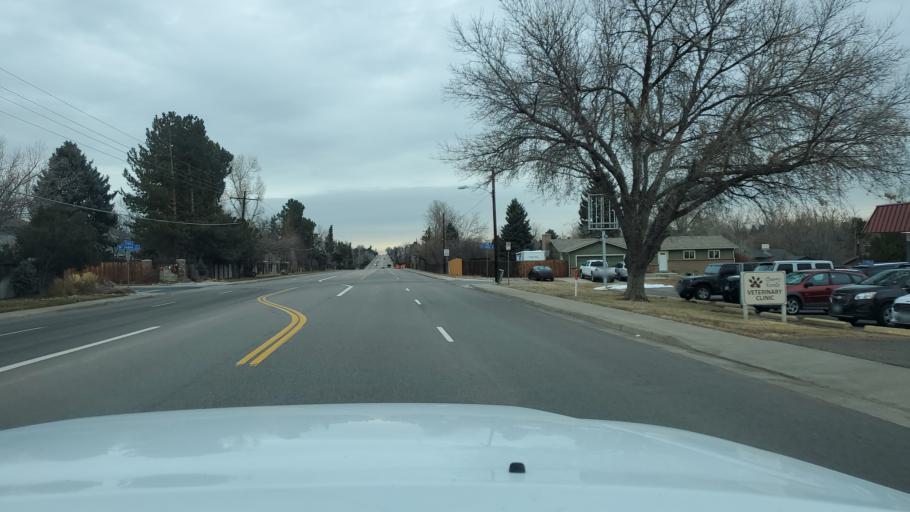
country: US
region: Colorado
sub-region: Arapahoe County
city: Southglenn
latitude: 39.5833
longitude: -104.9415
